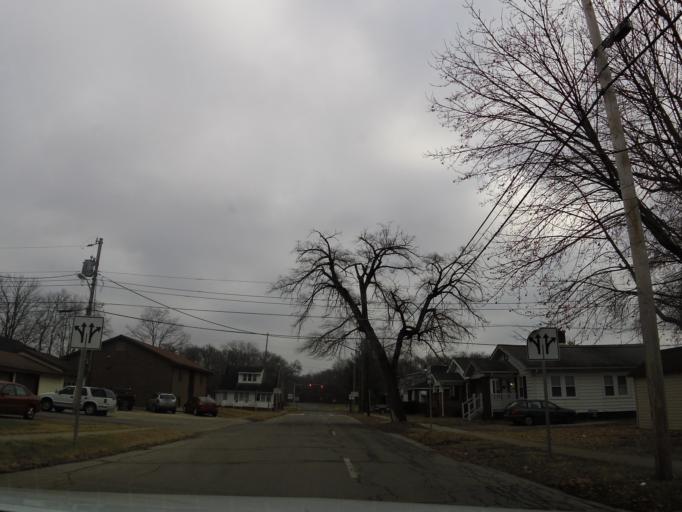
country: US
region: Indiana
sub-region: Bartholomew County
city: Columbus
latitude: 39.2073
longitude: -85.9055
